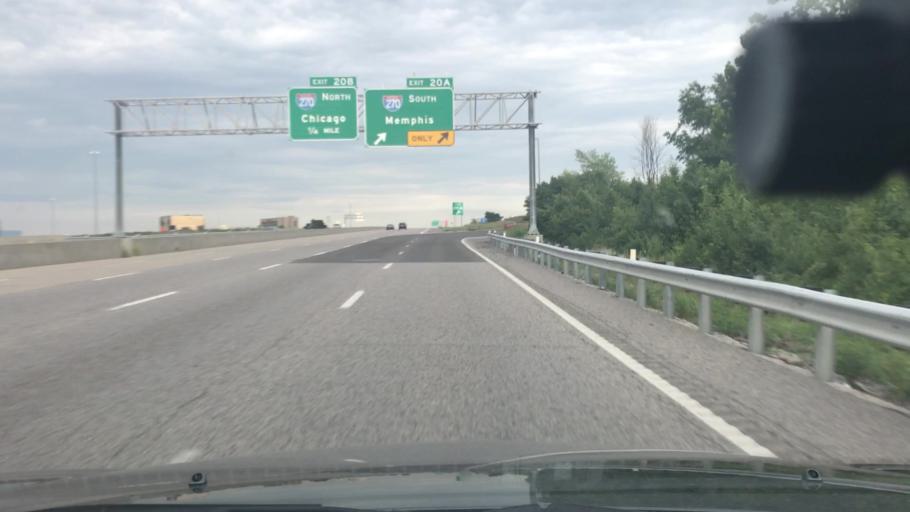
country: US
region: Missouri
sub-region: Saint Louis County
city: Maryland Heights
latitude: 38.6971
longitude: -90.4561
